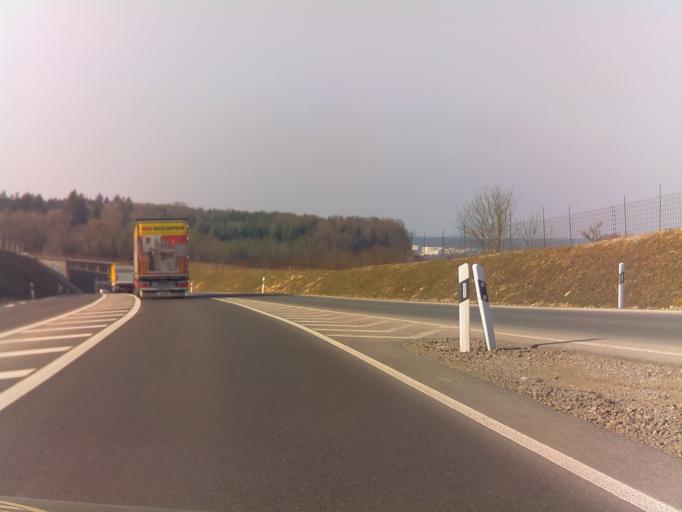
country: DE
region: Baden-Wuerttemberg
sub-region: Regierungsbezirk Stuttgart
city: Magstadt
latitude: 48.7465
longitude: 8.9483
